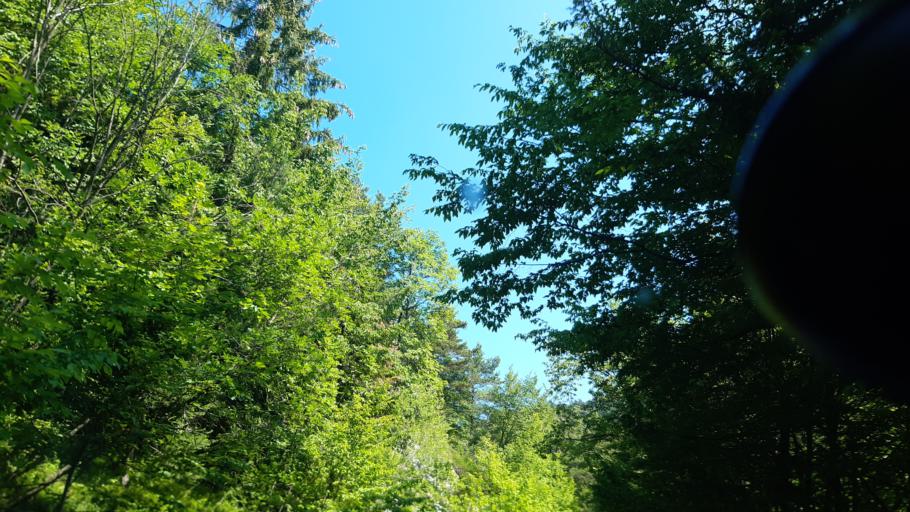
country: SI
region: Trzic
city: Bistrica pri Trzicu
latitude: 46.3648
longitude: 14.2787
